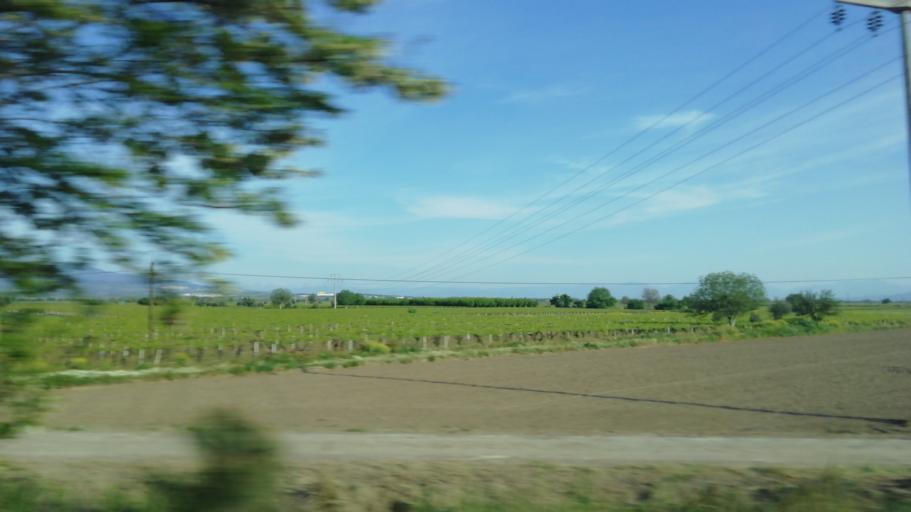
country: TR
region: Manisa
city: Saruhanli
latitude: 38.7175
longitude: 27.5554
